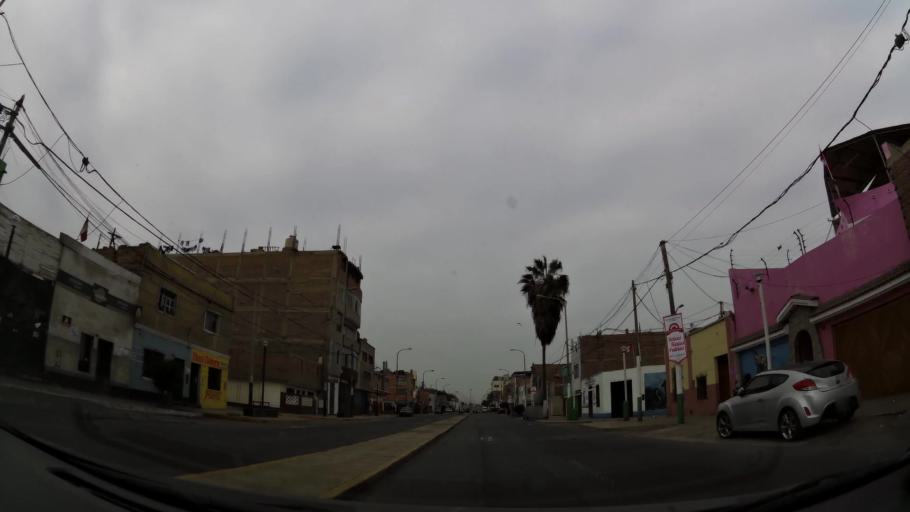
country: PE
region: Callao
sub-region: Callao
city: Callao
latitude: -12.0665
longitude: -77.1259
